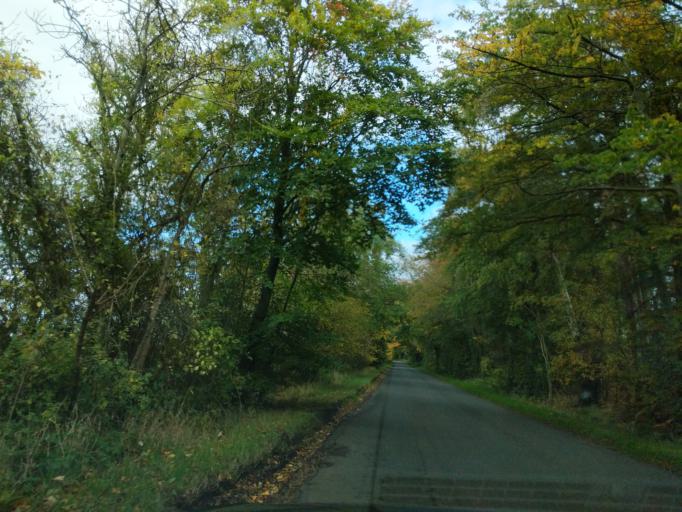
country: GB
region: Scotland
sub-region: East Lothian
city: Haddington
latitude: 55.9364
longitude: -2.7265
